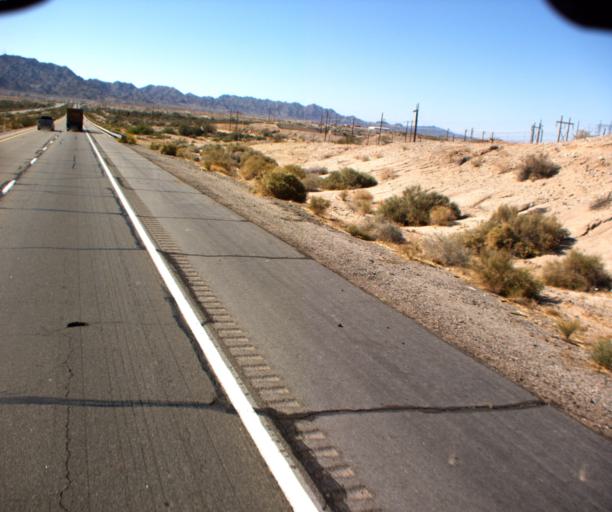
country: US
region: Arizona
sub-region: Yuma County
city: Wellton
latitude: 32.6623
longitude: -114.2635
